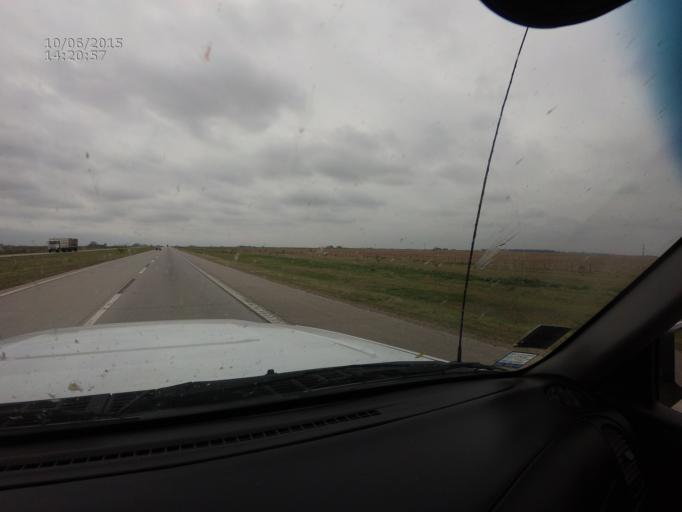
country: AR
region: Cordoba
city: Villa Maria
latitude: -32.3359
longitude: -63.2590
